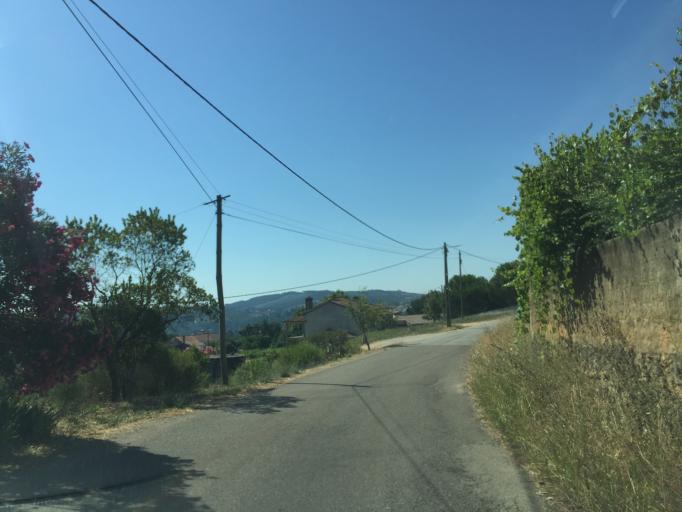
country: PT
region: Santarem
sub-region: Constancia
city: Constancia
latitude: 39.5558
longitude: -8.3155
